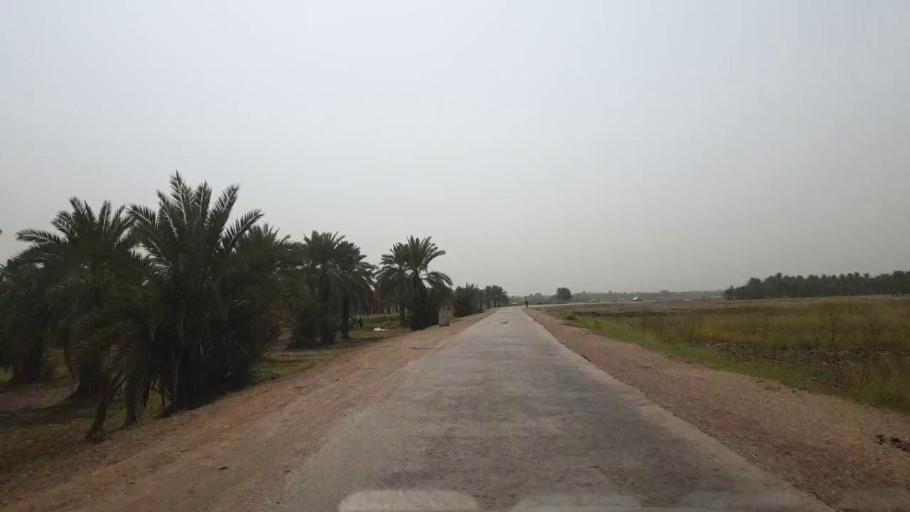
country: PK
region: Sindh
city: Gambat
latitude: 27.4263
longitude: 68.5394
